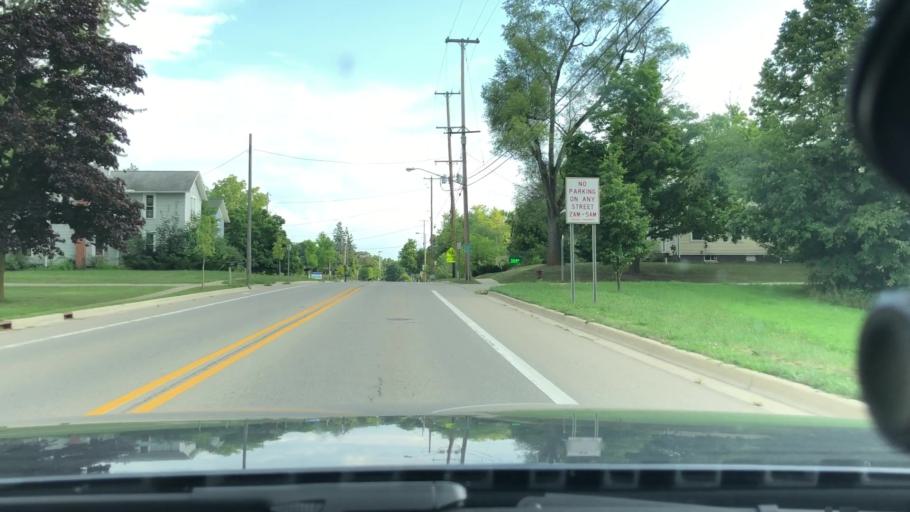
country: US
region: Michigan
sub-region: Washtenaw County
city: Manchester
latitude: 42.1569
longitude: -84.0411
